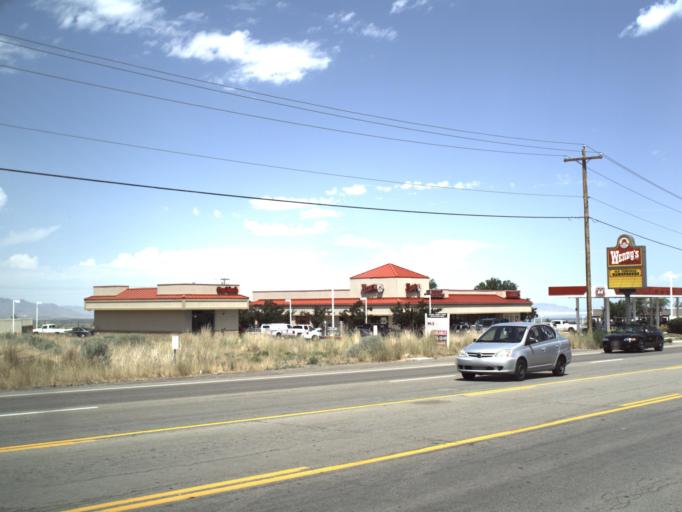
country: US
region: Utah
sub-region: Tooele County
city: Tooele
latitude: 40.5462
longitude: -112.2982
